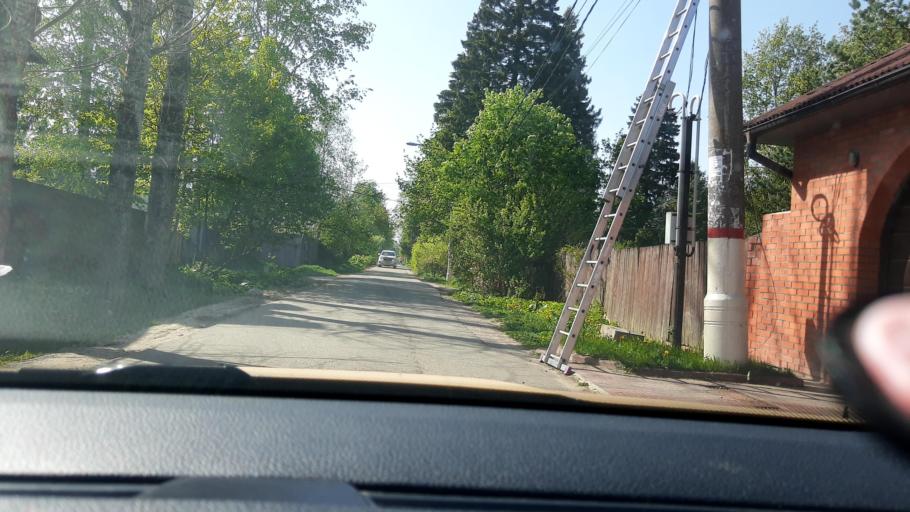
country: RU
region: Moskovskaya
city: Skhodnya
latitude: 55.9438
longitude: 37.3186
